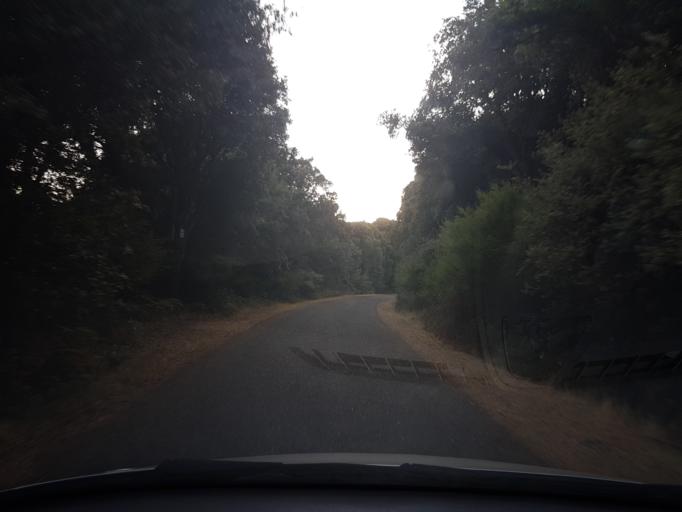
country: IT
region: Sardinia
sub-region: Provincia di Oristano
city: Seneghe
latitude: 40.1068
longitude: 8.5909
